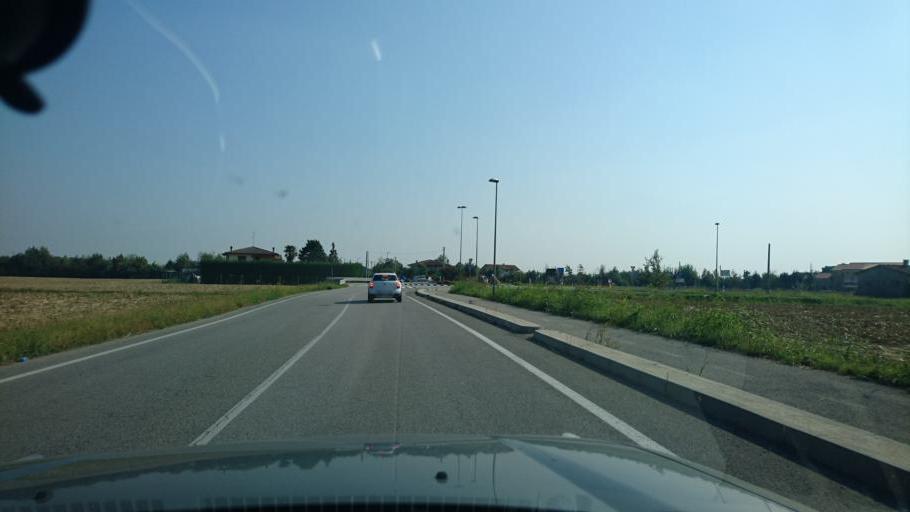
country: IT
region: Veneto
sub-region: Provincia di Padova
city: Ronchi di Campanile
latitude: 45.4586
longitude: 11.7780
